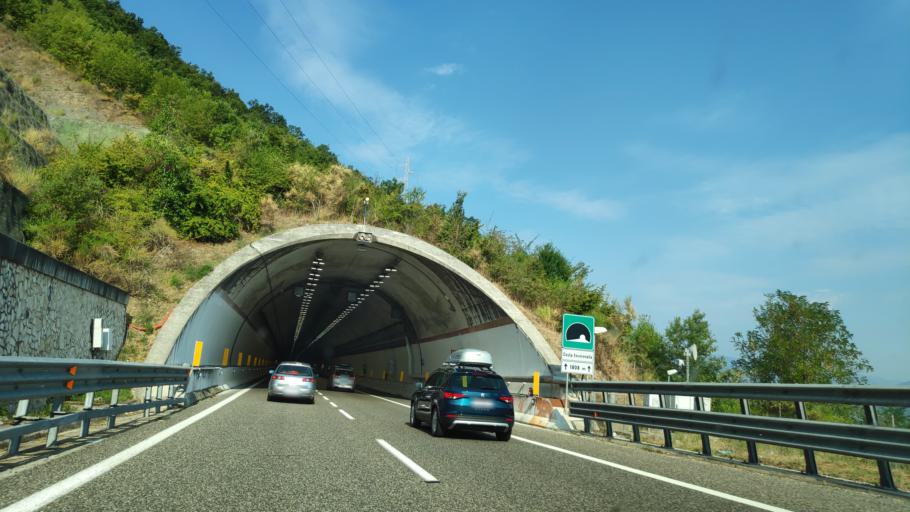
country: IT
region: Campania
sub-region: Provincia di Salerno
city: Petina
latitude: 40.5658
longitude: 15.3754
